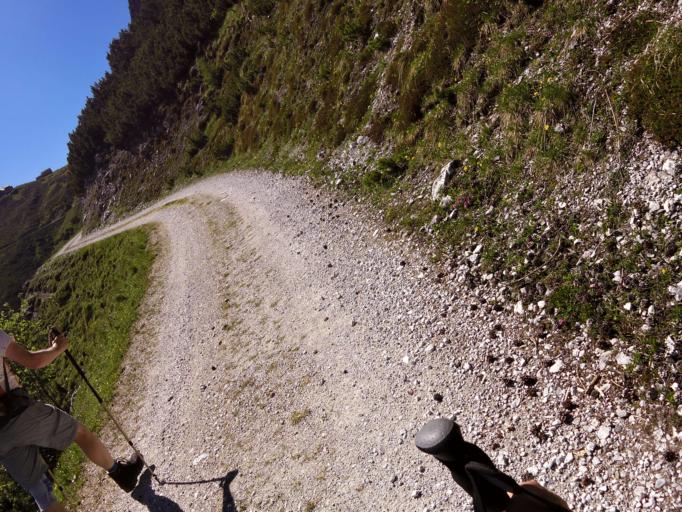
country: AT
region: Tyrol
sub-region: Politischer Bezirk Innsbruck Land
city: Neustift im Stubaital
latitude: 47.1273
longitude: 11.2886
